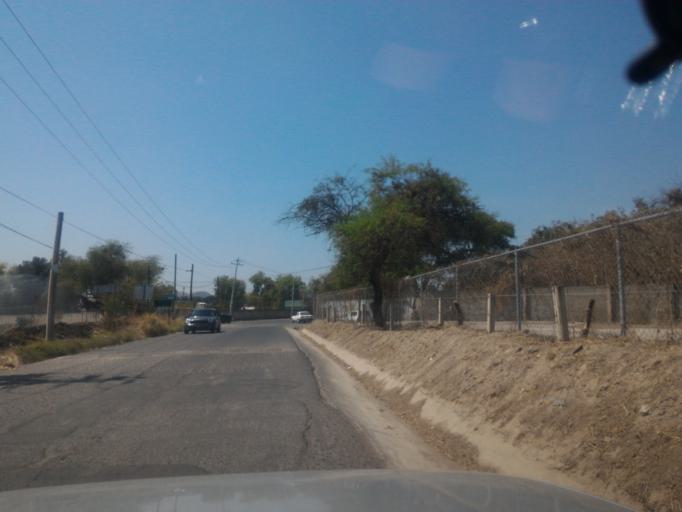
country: MX
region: Jalisco
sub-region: San Pedro Tlaquepaque
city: Santa Anita
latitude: 20.5518
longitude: -103.4338
